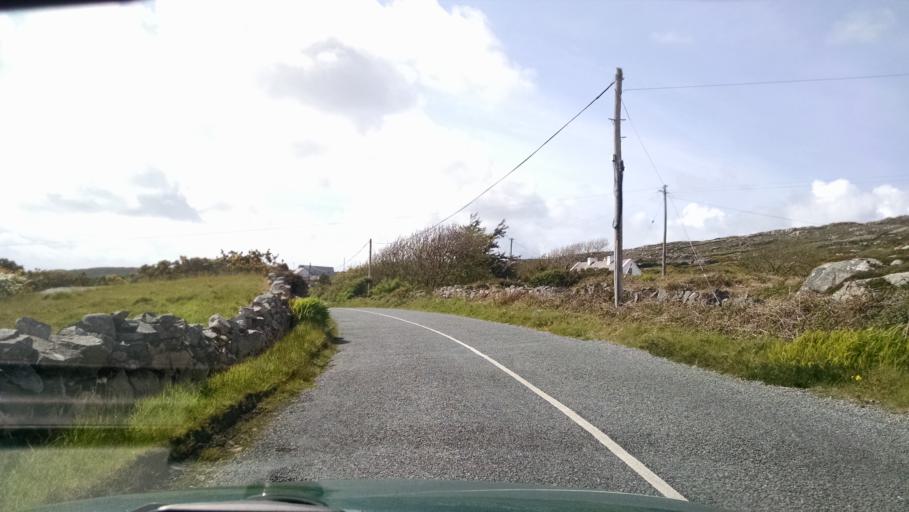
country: IE
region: Connaught
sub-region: County Galway
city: Clifden
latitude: 53.3854
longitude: -9.9583
